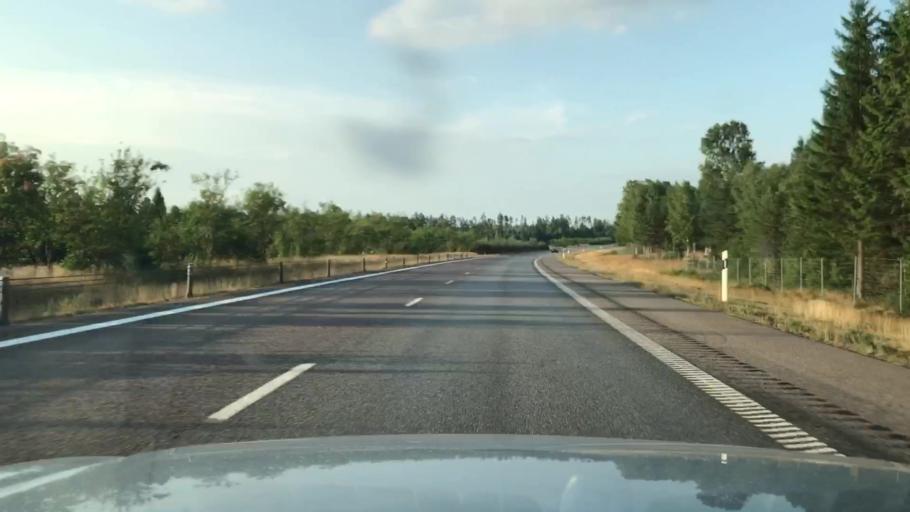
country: SE
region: Kronoberg
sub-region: Ljungby Kommun
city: Ljungby
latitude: 56.7413
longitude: 13.8539
